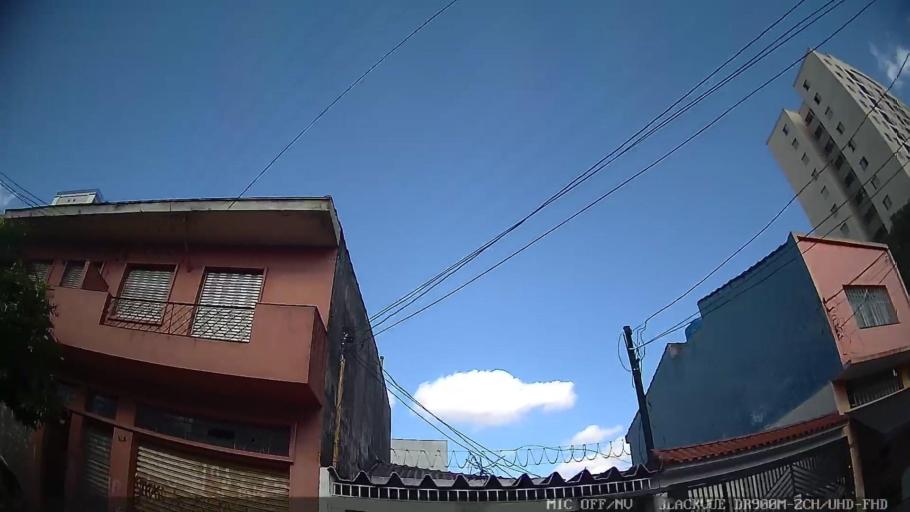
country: BR
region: Sao Paulo
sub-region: Sao Caetano Do Sul
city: Sao Caetano do Sul
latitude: -23.5968
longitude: -46.5995
